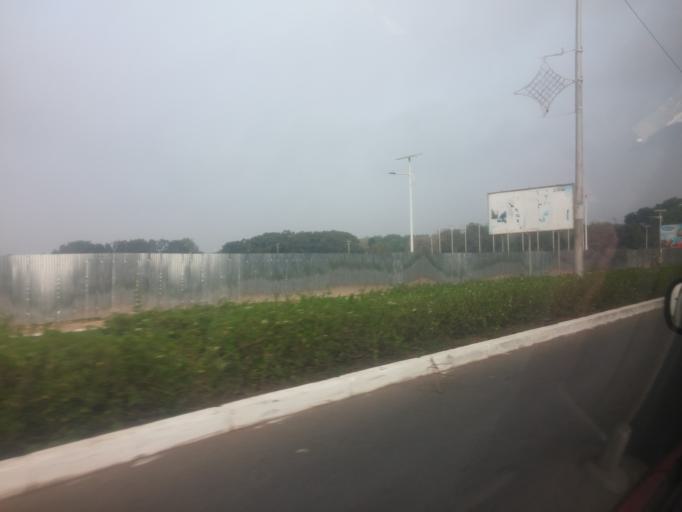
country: TG
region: Maritime
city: Lome
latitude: 6.1666
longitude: 1.2222
